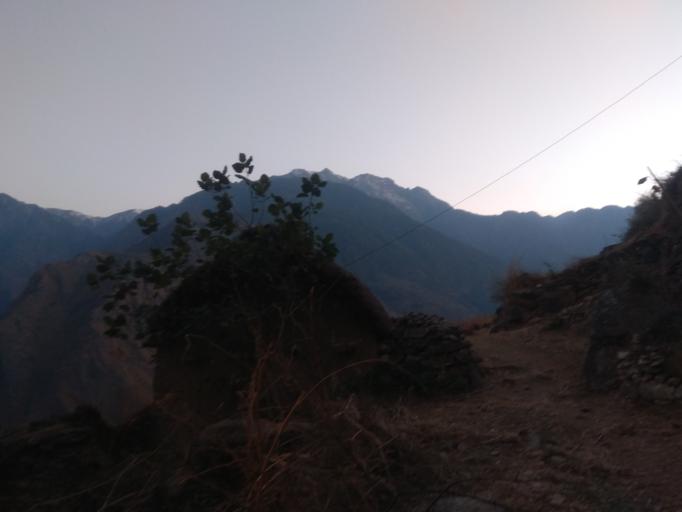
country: NP
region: Mid Western
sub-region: Bheri Zone
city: Dailekh
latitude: 29.2696
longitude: 81.6942
